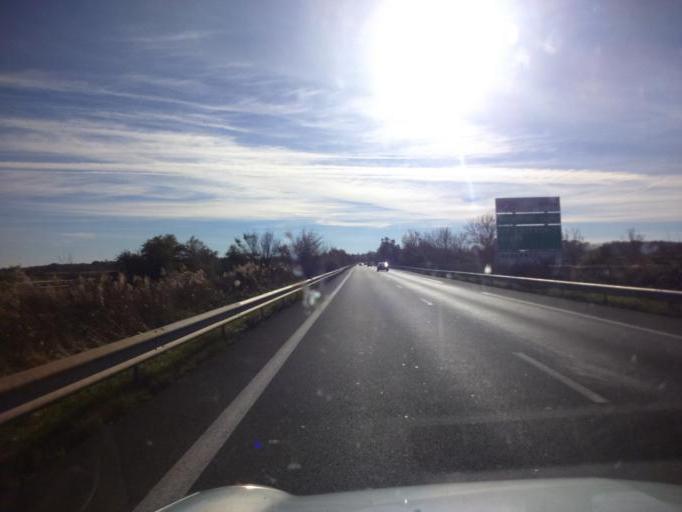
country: FR
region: Poitou-Charentes
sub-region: Departement de la Charente-Maritime
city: Breuil-Magne
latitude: 45.9770
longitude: -0.9943
